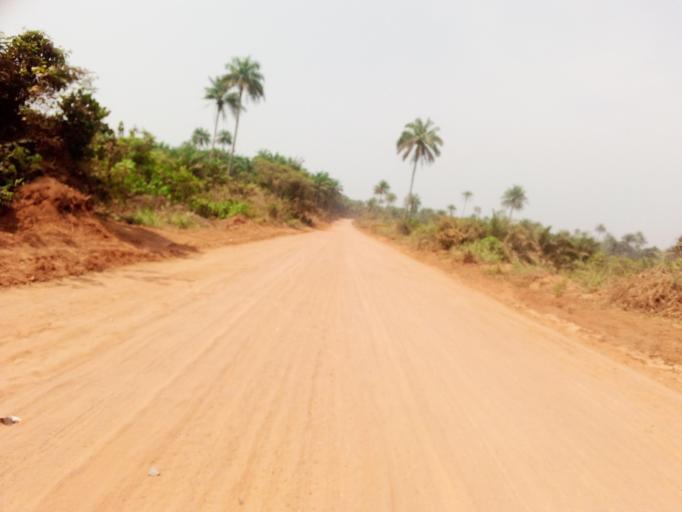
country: SL
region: Southern Province
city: Sumbuya
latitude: 7.6198
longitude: -12.1171
